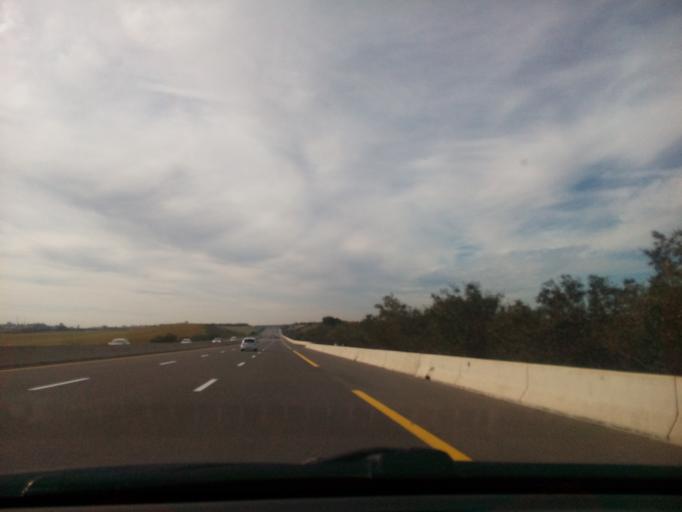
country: DZ
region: Sidi Bel Abbes
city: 'Ain el Berd
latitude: 35.3141
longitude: -0.5476
